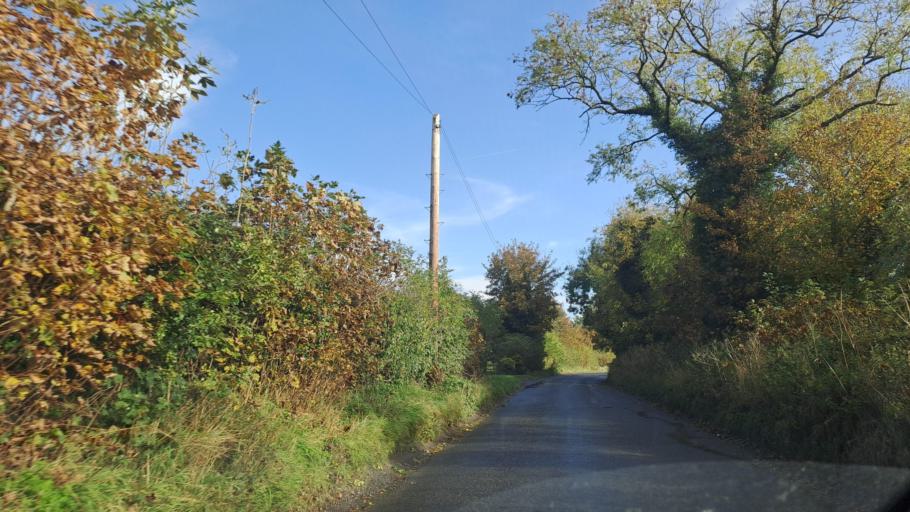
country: IE
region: Ulster
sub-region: County Monaghan
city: Carrickmacross
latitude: 53.8773
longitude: -6.6751
